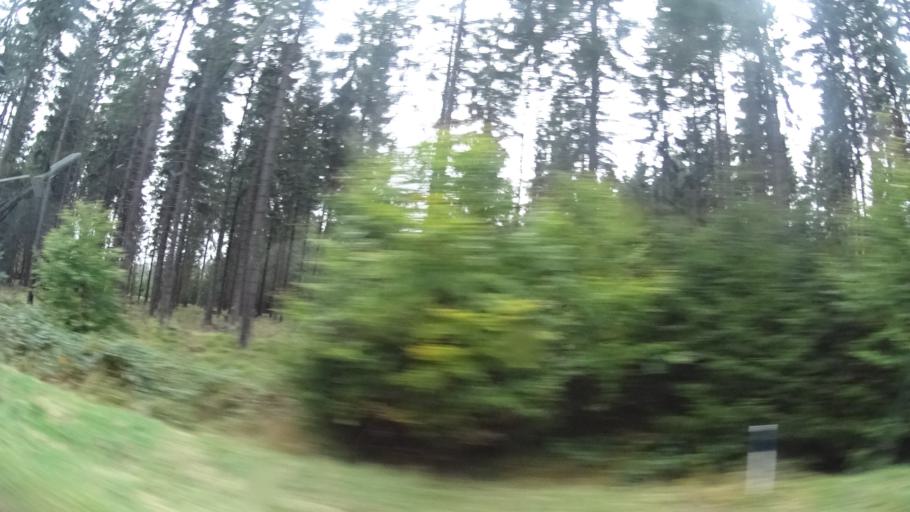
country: DE
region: Bavaria
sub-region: Upper Franconia
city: Tschirn
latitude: 50.4244
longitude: 11.4582
